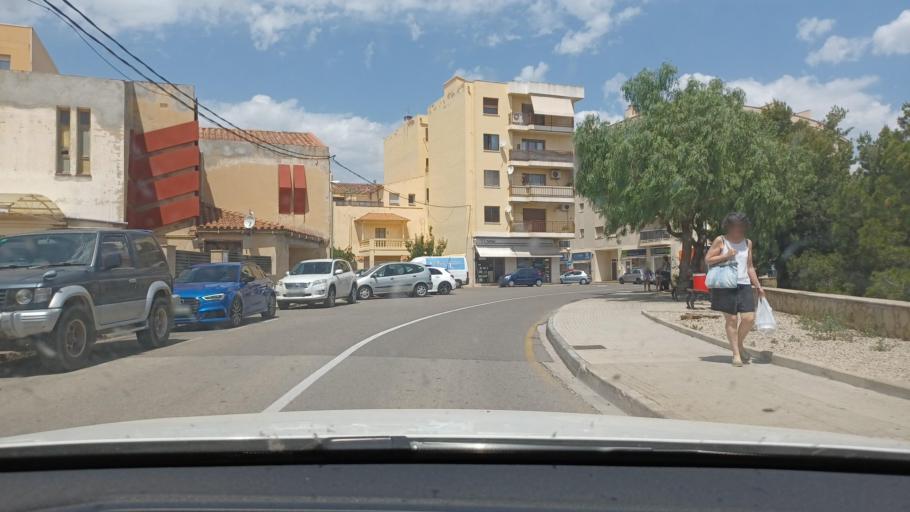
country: ES
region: Catalonia
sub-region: Provincia de Tarragona
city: Colldejou
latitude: 40.9921
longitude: 0.9242
